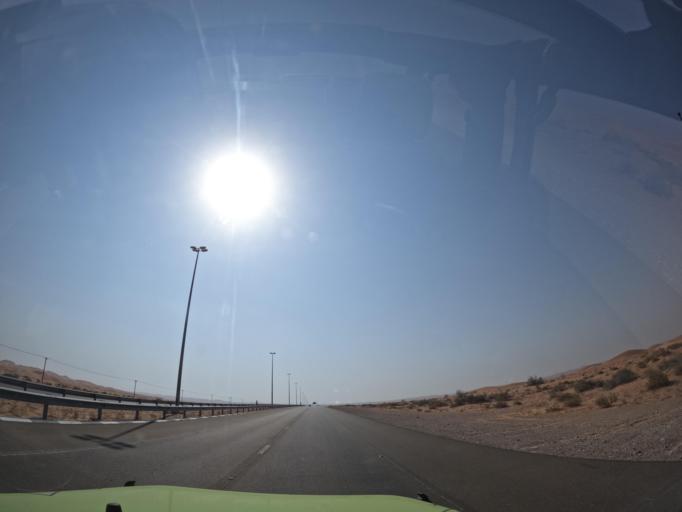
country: OM
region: Al Buraimi
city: Al Buraymi
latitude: 24.4470
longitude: 55.6572
